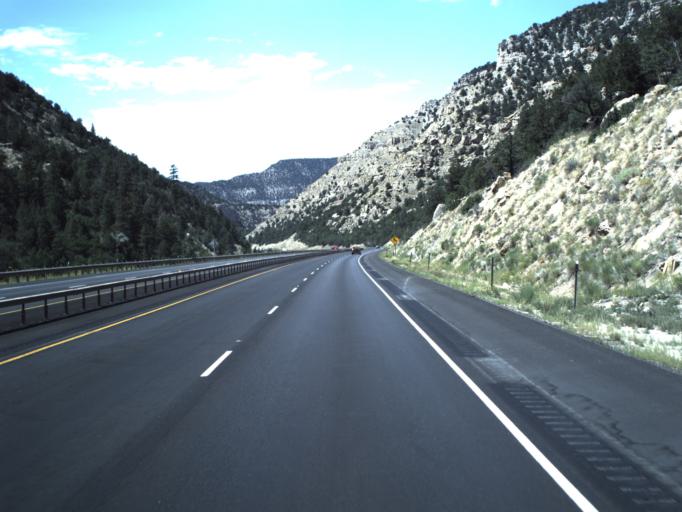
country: US
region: Utah
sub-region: Sevier County
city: Salina
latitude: 38.8884
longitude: -111.6105
